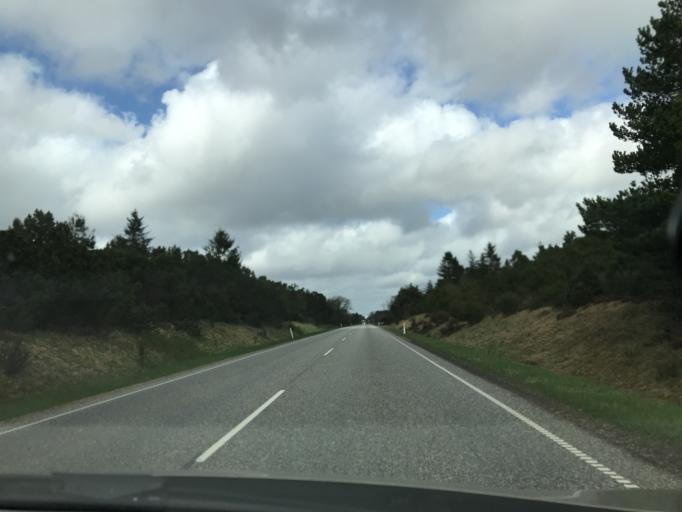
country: DK
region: Central Jutland
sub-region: Herning Kommune
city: Sunds
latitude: 56.3750
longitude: 8.9849
